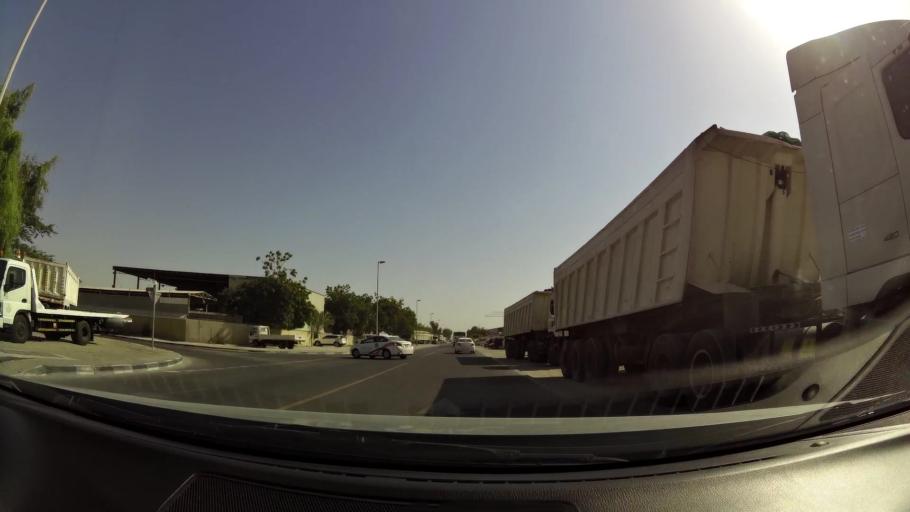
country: AE
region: Dubai
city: Dubai
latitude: 25.1290
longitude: 55.2258
